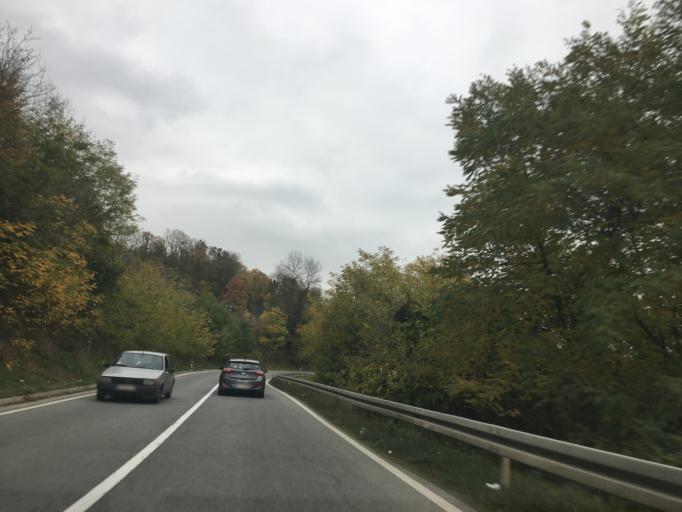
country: RS
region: Central Serbia
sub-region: Raski Okrug
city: Kraljevo
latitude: 43.7299
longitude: 20.7488
